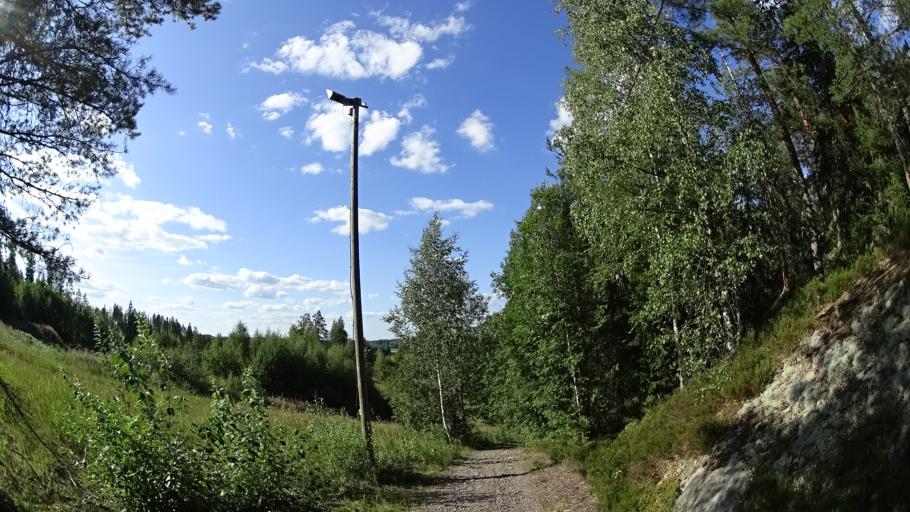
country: FI
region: Uusimaa
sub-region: Helsinki
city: Vihti
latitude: 60.3769
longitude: 24.3711
